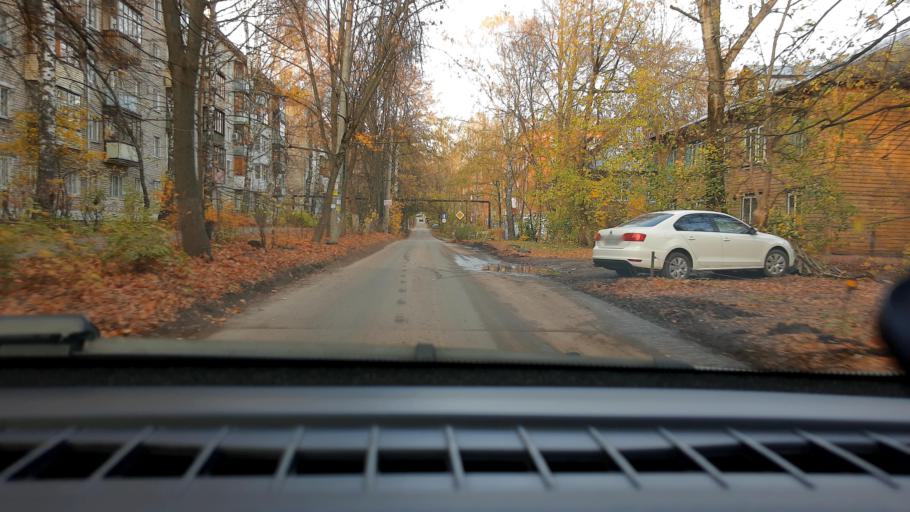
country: RU
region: Nizjnij Novgorod
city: Nizhniy Novgorod
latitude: 56.2785
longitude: 43.9866
